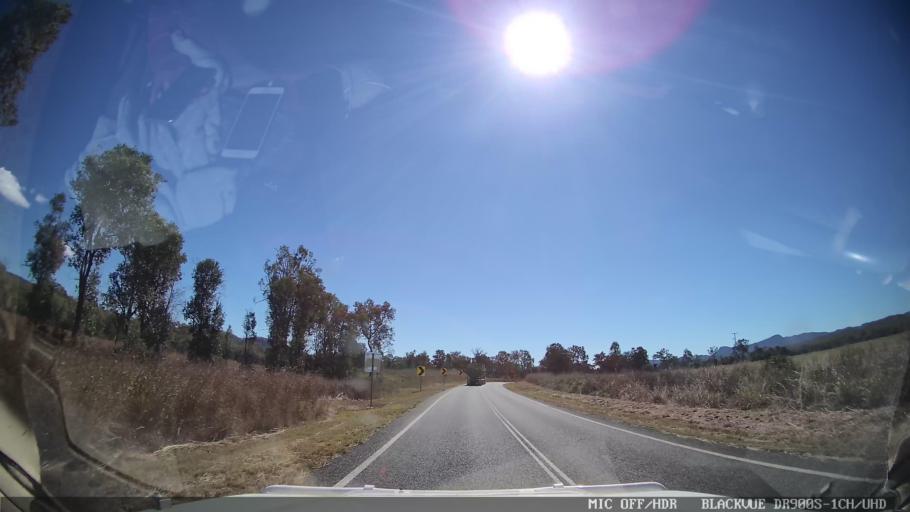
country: AU
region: Queensland
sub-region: Gladstone
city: Toolooa
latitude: -24.2780
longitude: 151.2769
